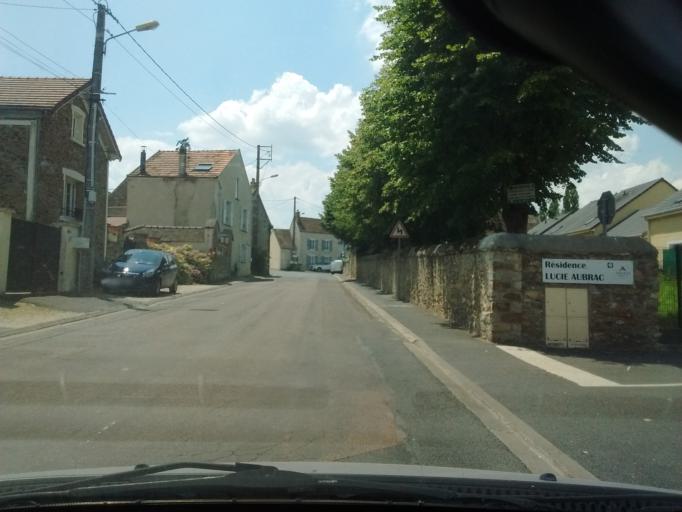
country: FR
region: Ile-de-France
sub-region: Departement de Seine-et-Marne
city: Ponthierry
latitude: 48.5227
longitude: 2.5397
